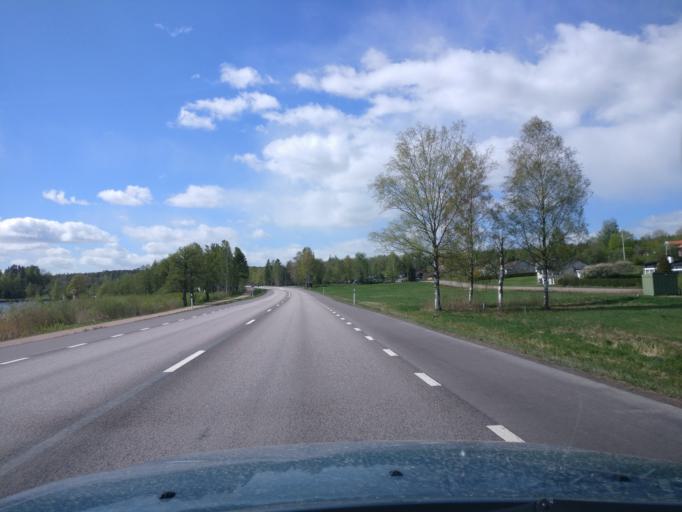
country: SE
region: Vaermland
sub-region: Karlstads Kommun
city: Molkom
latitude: 59.5958
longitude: 13.7077
